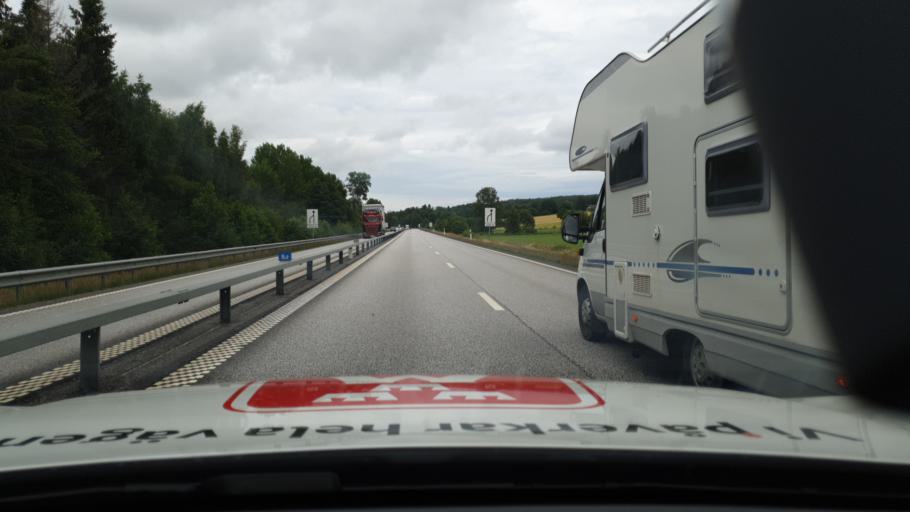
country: SE
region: Joenkoeping
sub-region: Jonkopings Kommun
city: Bankeryd
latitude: 57.8106
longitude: 14.0992
